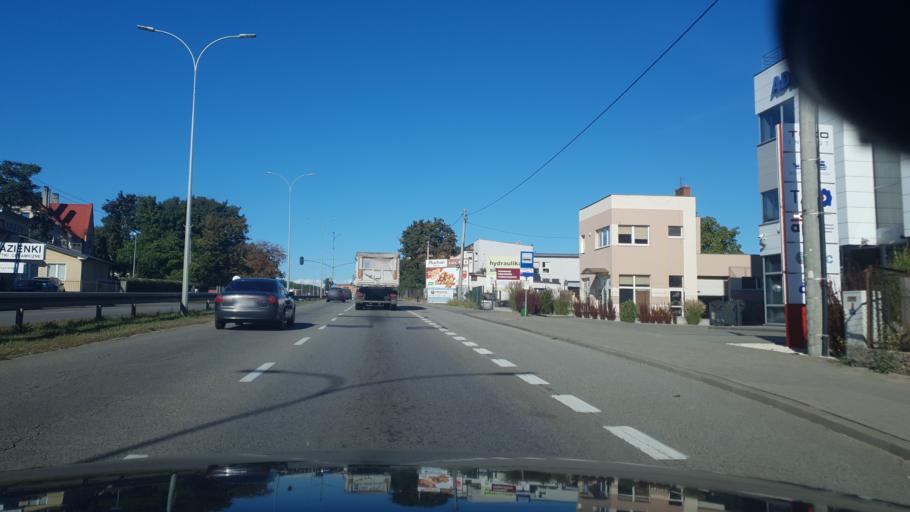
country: PL
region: Pomeranian Voivodeship
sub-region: Powiat wejherowski
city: Rumia
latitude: 54.5607
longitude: 18.4010
